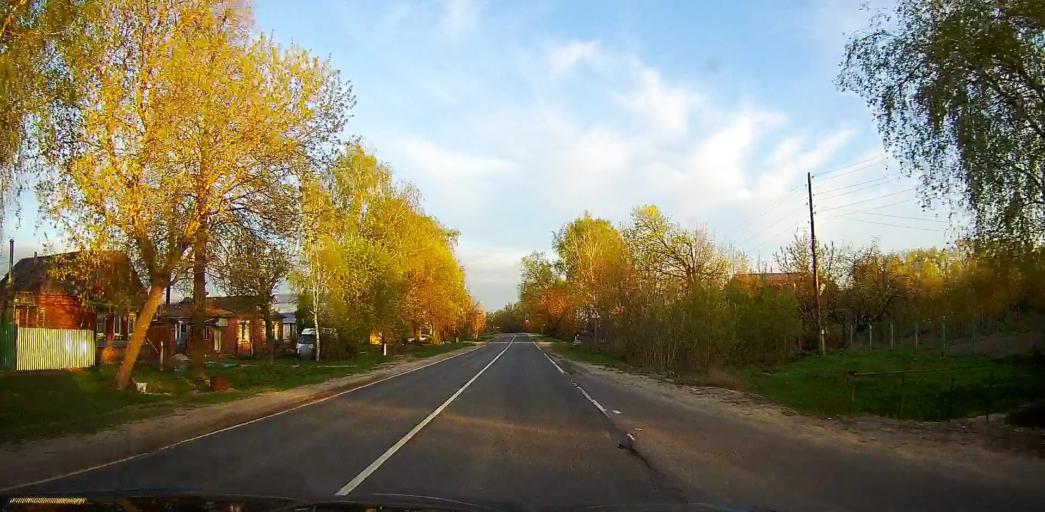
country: RU
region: Moskovskaya
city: Peski
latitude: 55.2120
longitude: 38.6738
